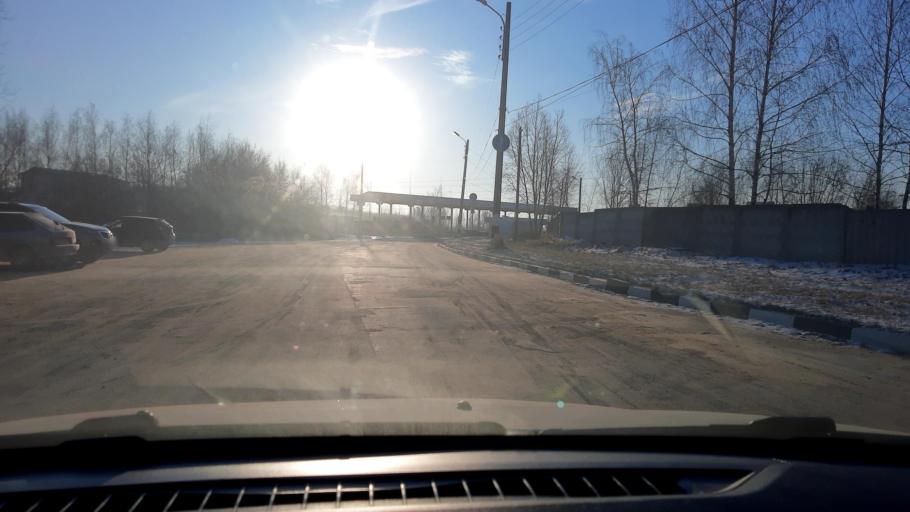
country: RU
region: Nizjnij Novgorod
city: Nizhniy Novgorod
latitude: 56.2935
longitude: 43.8874
